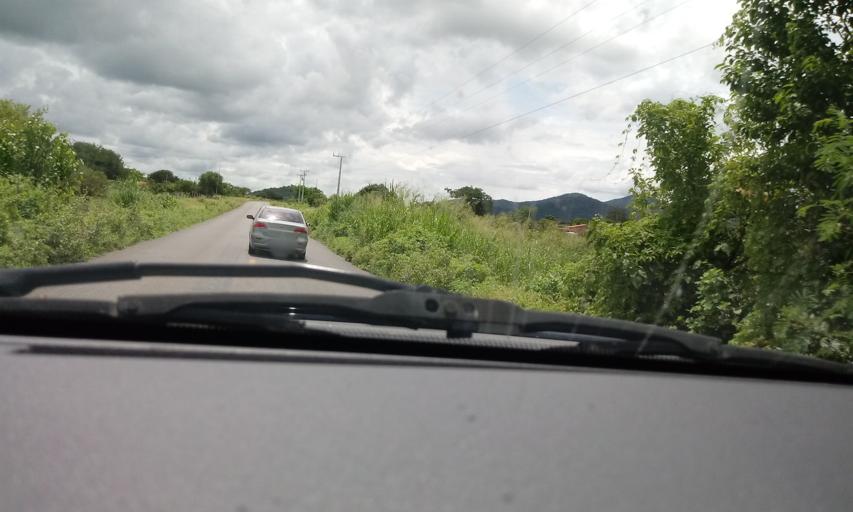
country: BR
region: Bahia
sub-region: Guanambi
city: Guanambi
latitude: -14.1281
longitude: -42.8523
